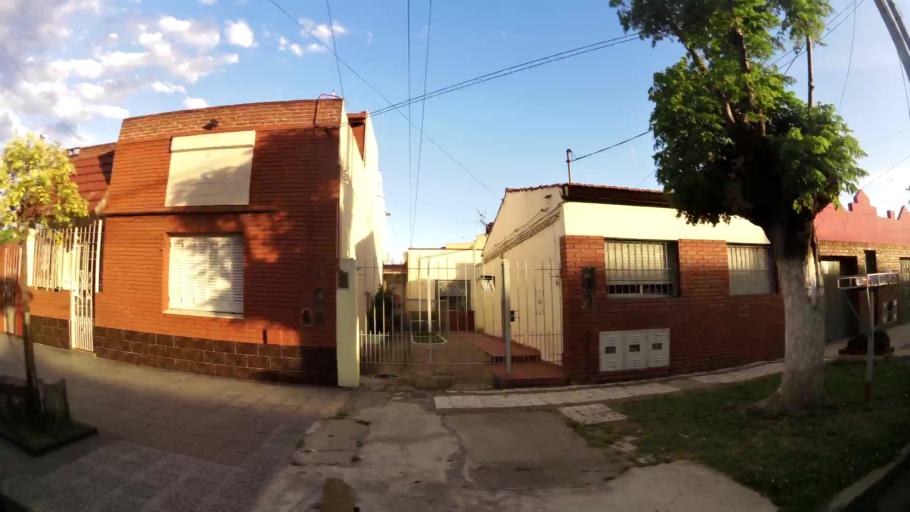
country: AR
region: Buenos Aires
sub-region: Partido de Avellaneda
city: Avellaneda
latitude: -34.6984
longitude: -58.3368
